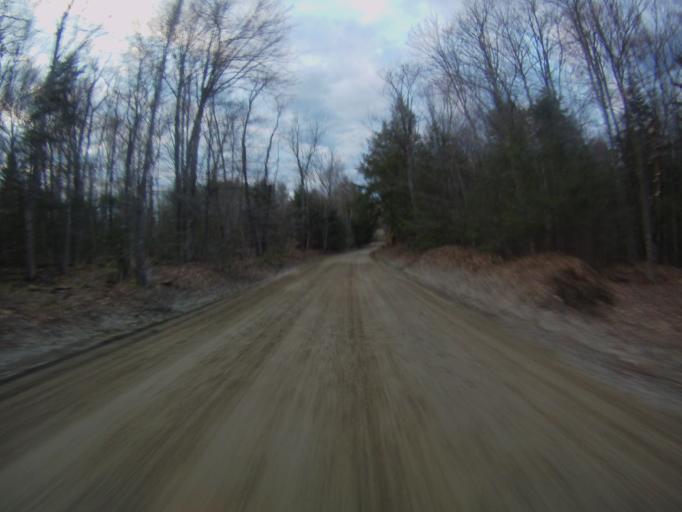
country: US
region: Vermont
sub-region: Rutland County
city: Brandon
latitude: 43.9406
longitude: -73.0221
